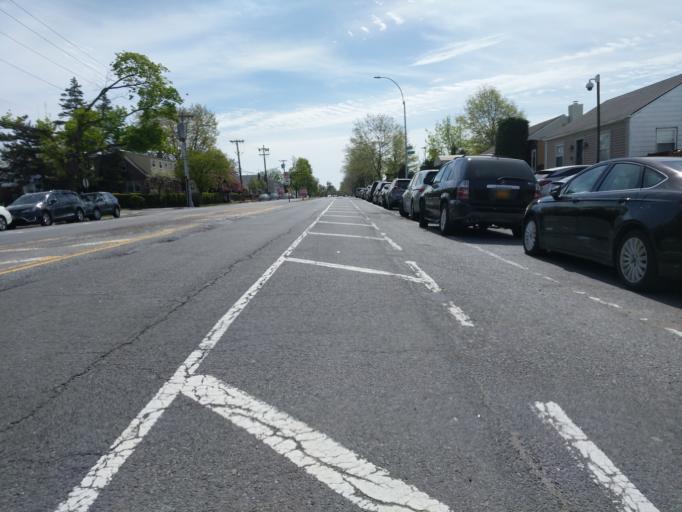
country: US
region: New York
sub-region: Nassau County
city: Elmont
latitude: 40.6868
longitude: -73.7380
